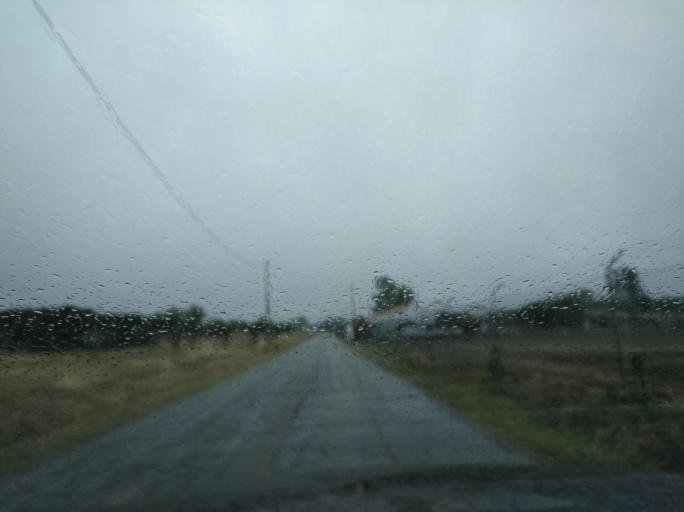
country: PT
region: Portalegre
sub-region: Campo Maior
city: Campo Maior
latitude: 38.9824
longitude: -7.0688
